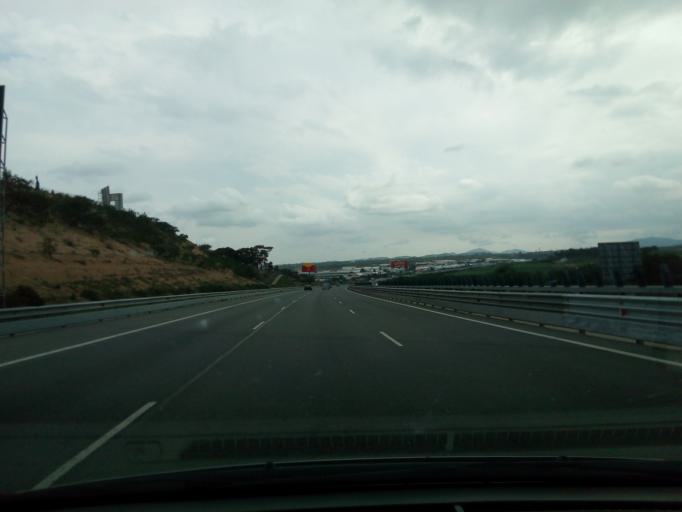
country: CY
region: Lefkosia
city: Dali
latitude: 35.0622
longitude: 33.3818
